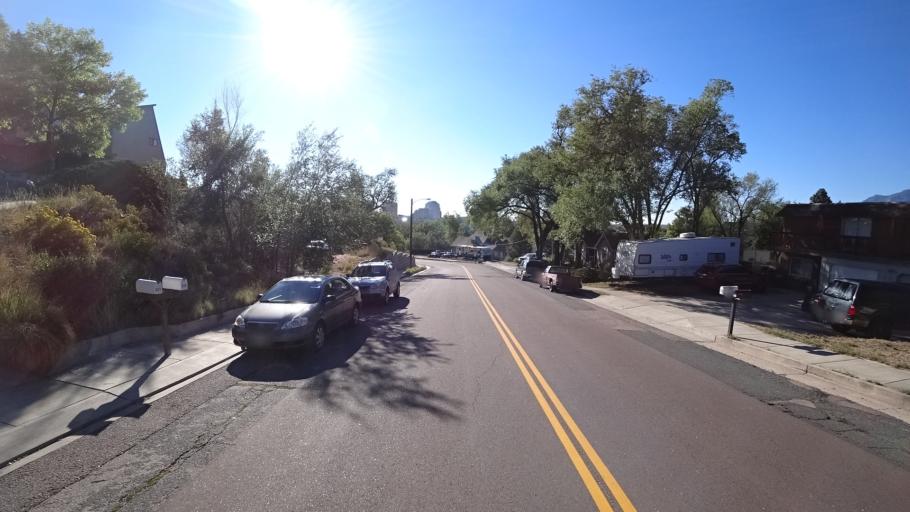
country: US
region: Colorado
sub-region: El Paso County
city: Colorado Springs
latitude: 38.8395
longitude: -104.8369
